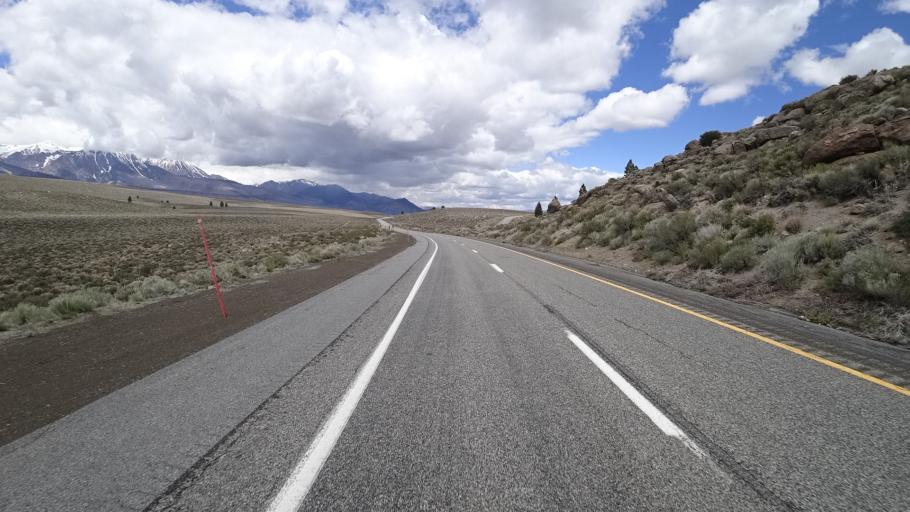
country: US
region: California
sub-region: Mono County
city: Mammoth Lakes
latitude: 37.8344
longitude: -119.0731
